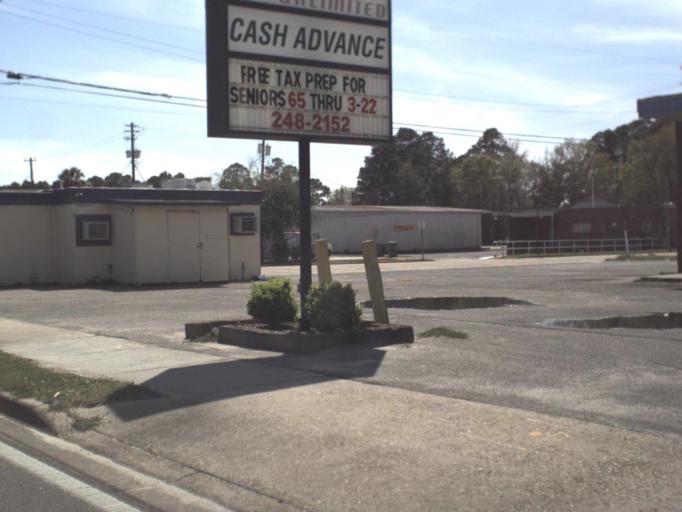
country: US
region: Florida
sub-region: Bay County
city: Lynn Haven
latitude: 30.2469
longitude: -85.6487
